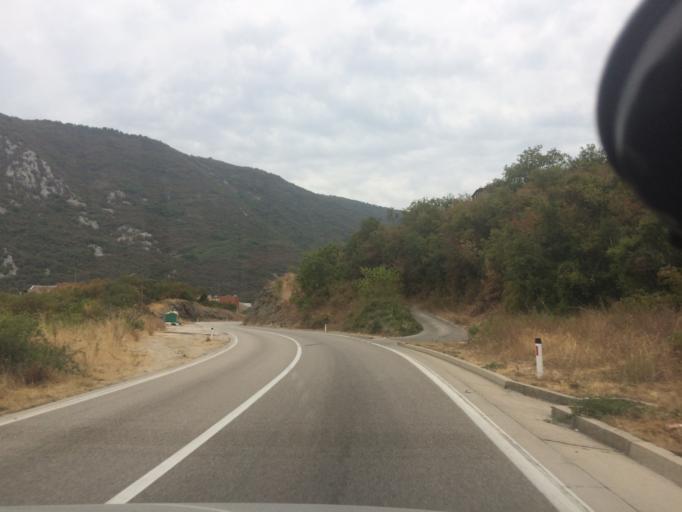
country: ME
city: Lipci
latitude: 42.4924
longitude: 18.6481
